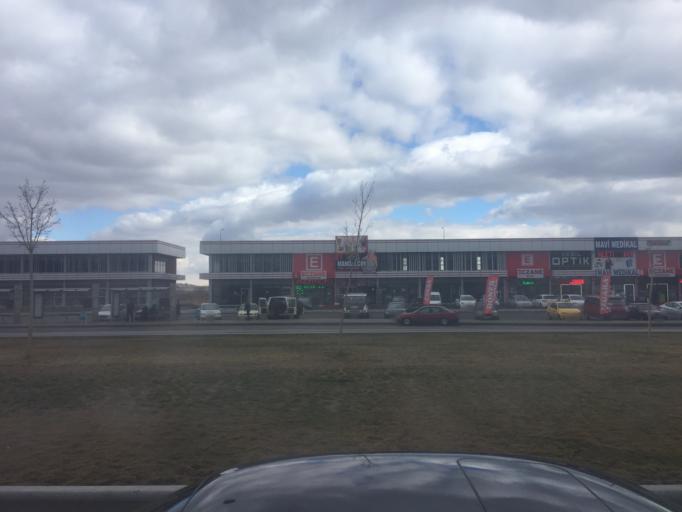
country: TR
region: Kayseri
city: Melikgazi
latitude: 38.7708
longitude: 35.4126
